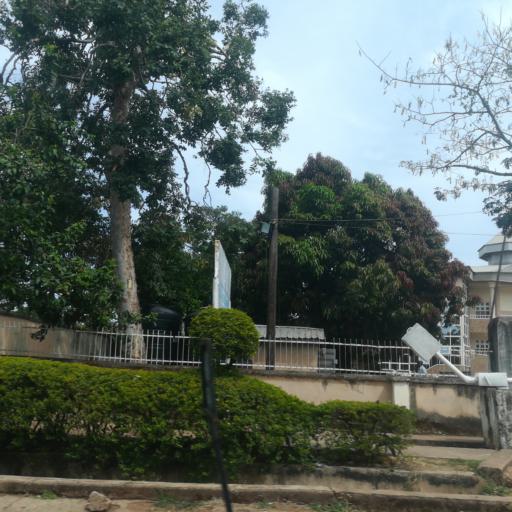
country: NG
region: Plateau
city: Jos
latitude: 9.9108
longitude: 8.8872
